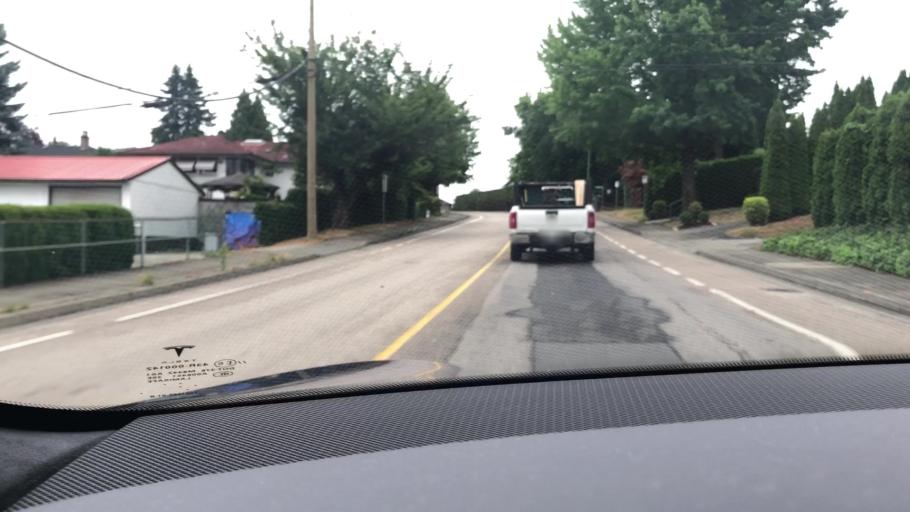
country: CA
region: British Columbia
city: Burnaby
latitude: 49.2293
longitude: -122.9673
